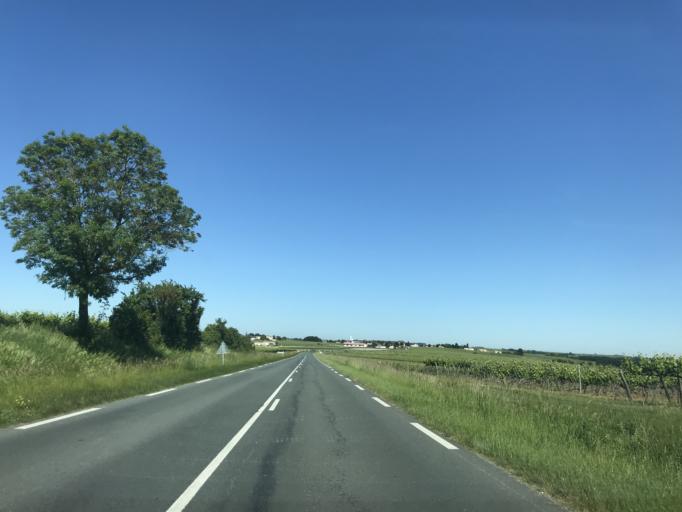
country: FR
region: Poitou-Charentes
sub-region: Departement de la Charente
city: Chateaubernard
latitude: 45.5525
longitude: -0.3674
